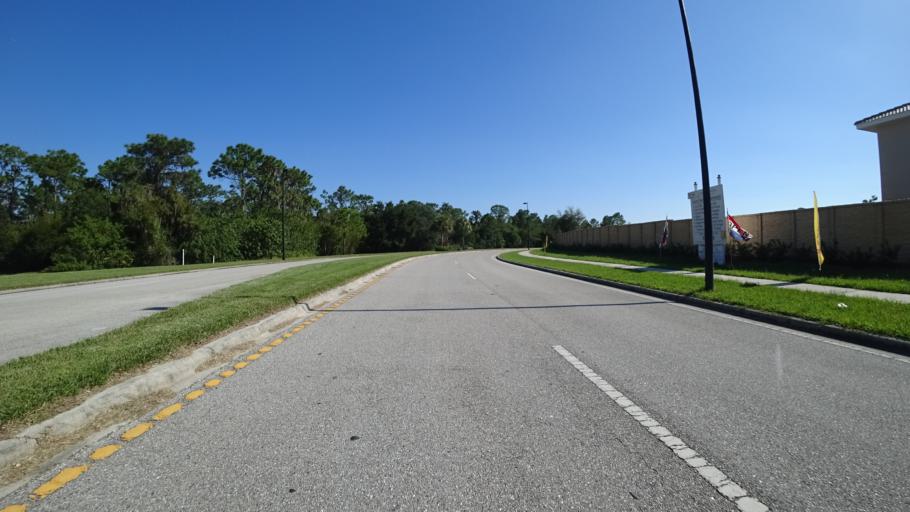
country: US
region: Florida
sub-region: Sarasota County
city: The Meadows
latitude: 27.4009
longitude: -82.4478
